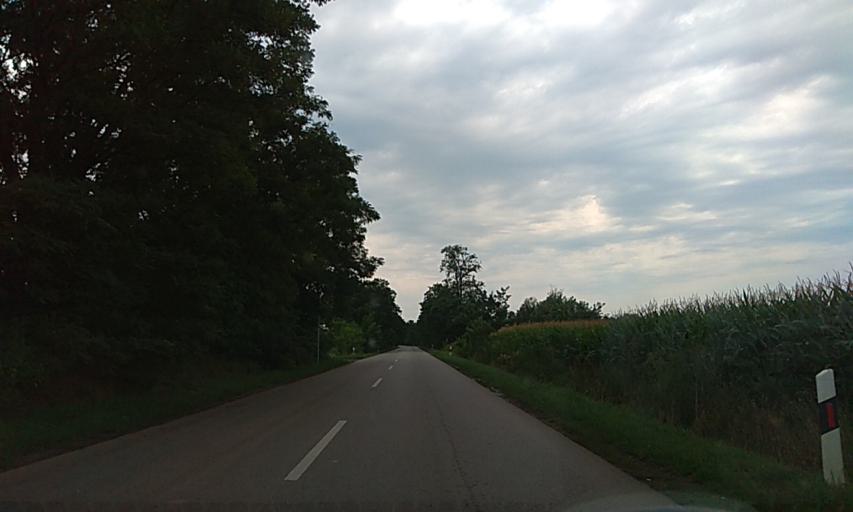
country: HU
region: Szabolcs-Szatmar-Bereg
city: Buj
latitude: 48.0878
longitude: 21.6410
